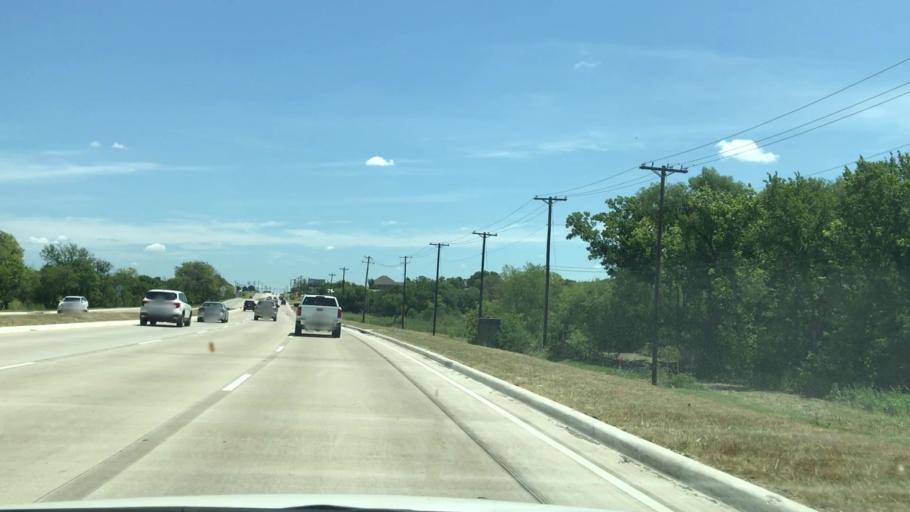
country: US
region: Texas
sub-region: Collin County
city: Lavon
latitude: 33.0215
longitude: -96.4685
